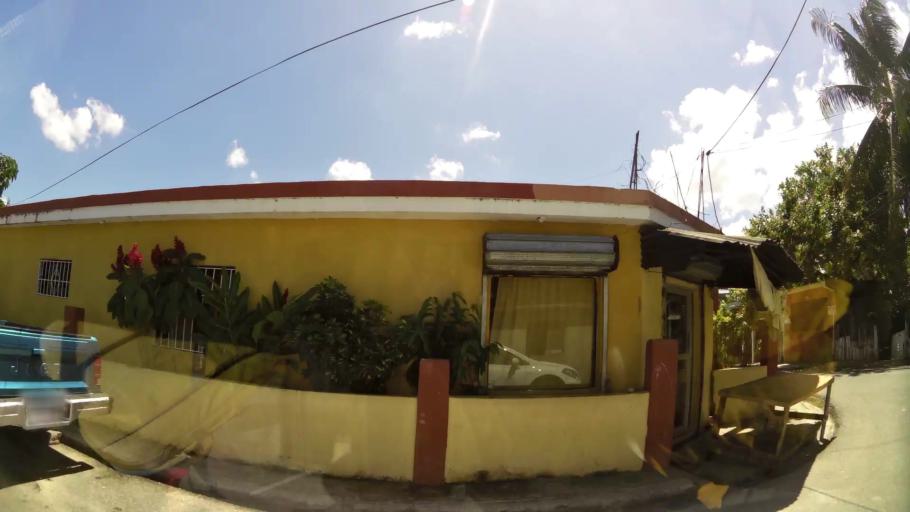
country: DO
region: San Cristobal
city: San Cristobal
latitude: 18.3994
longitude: -70.1110
